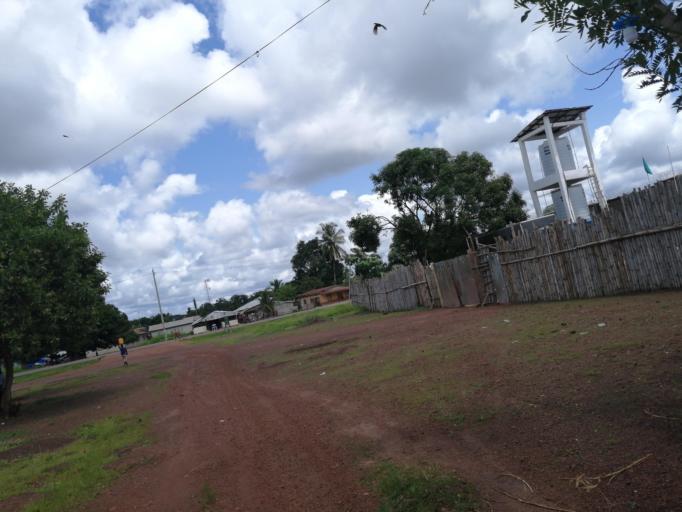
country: SL
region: Northern Province
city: Port Loko
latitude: 8.7753
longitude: -12.7887
